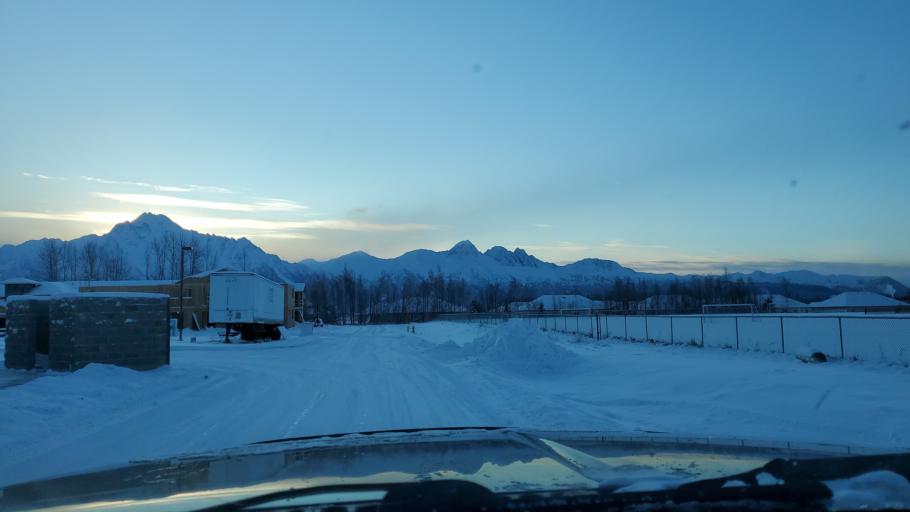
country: US
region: Alaska
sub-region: Matanuska-Susitna Borough
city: Palmer
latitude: 61.5903
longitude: -149.1057
